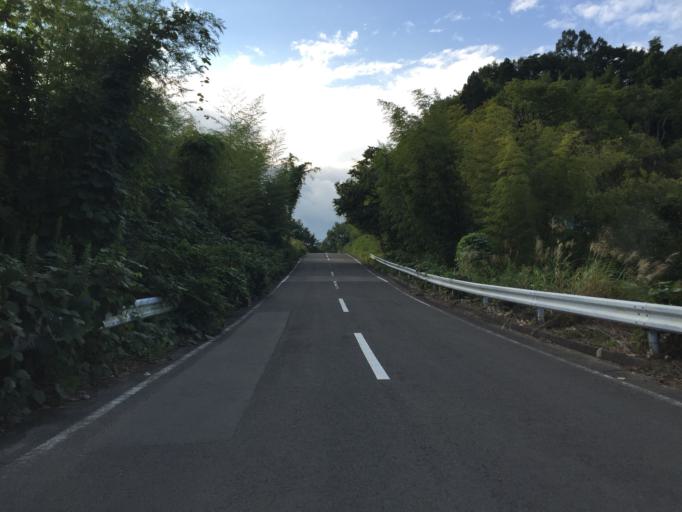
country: JP
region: Fukushima
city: Fukushima-shi
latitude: 37.6559
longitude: 140.5560
